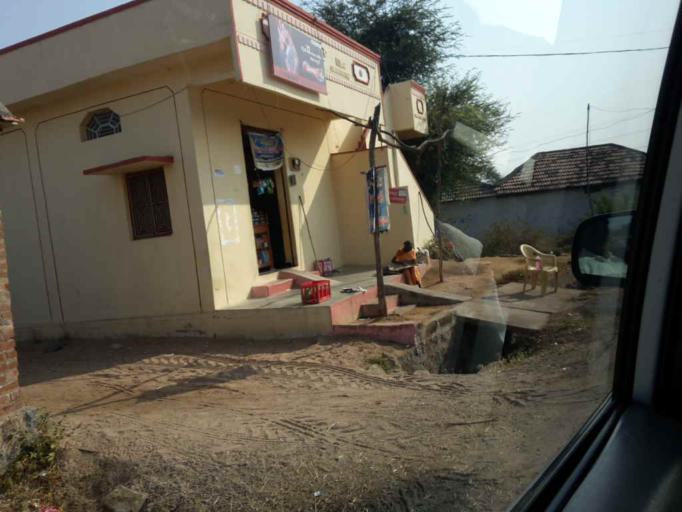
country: IN
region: Telangana
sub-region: Karimnagar
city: Vemalwada
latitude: 18.4012
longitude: 78.9862
